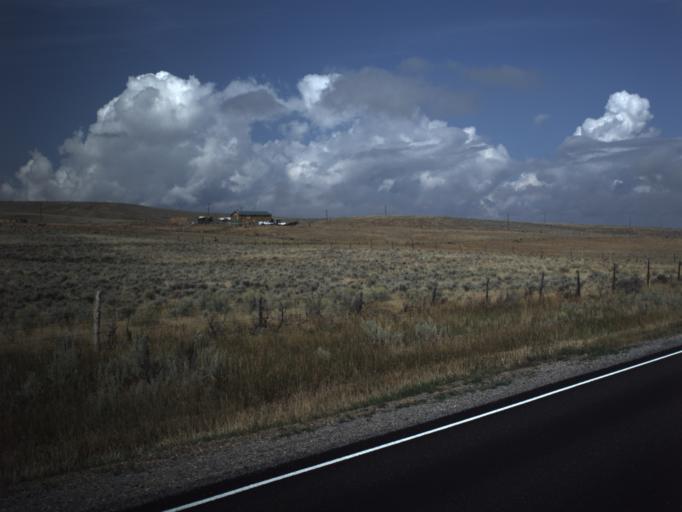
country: US
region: Utah
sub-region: Rich County
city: Randolph
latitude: 41.6034
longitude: -111.1764
